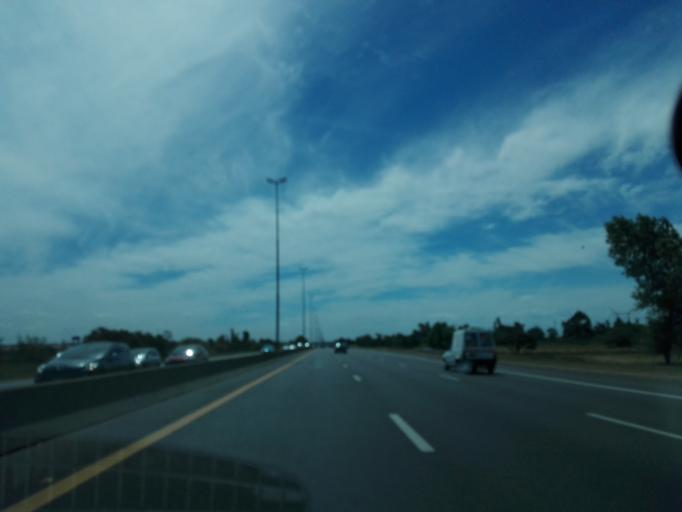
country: AR
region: Buenos Aires
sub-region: Partido de Quilmes
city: Quilmes
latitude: -34.7607
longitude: -58.1811
